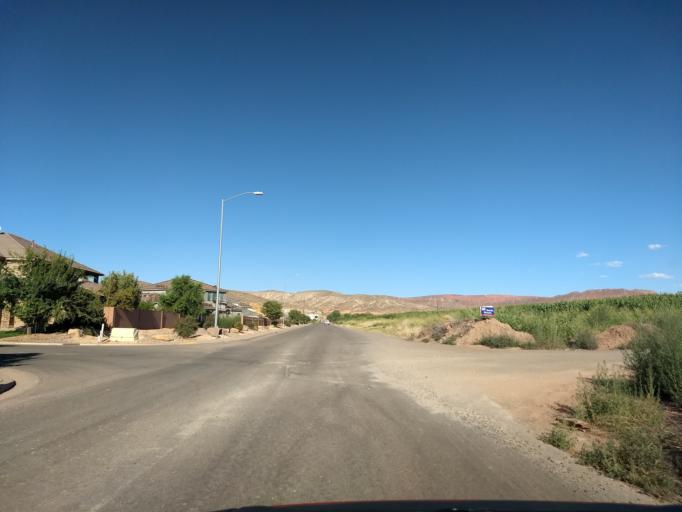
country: US
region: Utah
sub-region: Washington County
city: Washington
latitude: 37.0959
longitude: -113.5139
